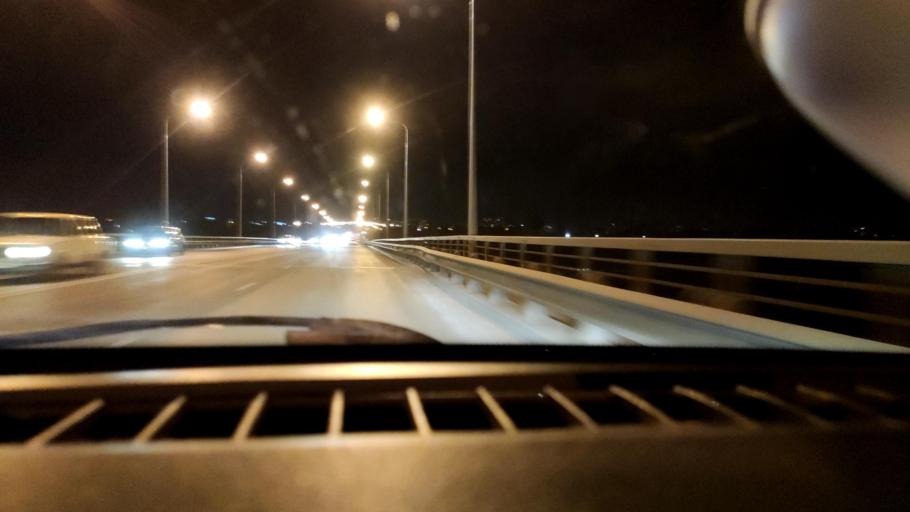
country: RU
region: Samara
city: Samara
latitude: 53.1682
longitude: 50.1963
